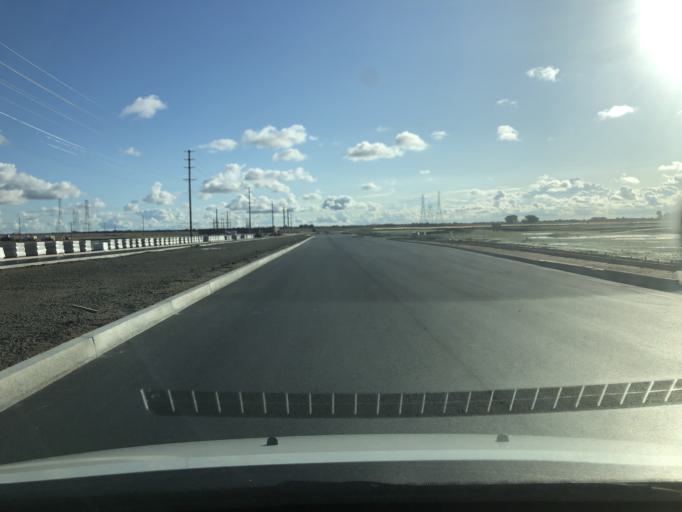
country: US
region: California
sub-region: Sacramento County
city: Antelope
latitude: 38.7691
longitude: -121.3855
